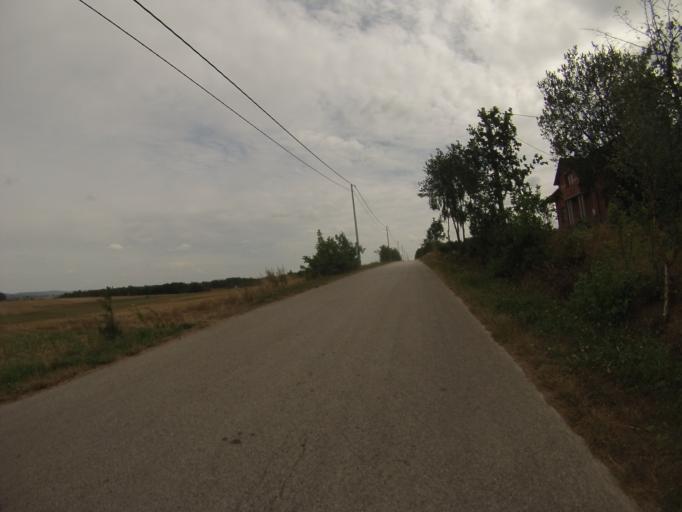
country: PL
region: Swietokrzyskie
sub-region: Powiat kielecki
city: Lagow
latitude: 50.7590
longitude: 21.0915
